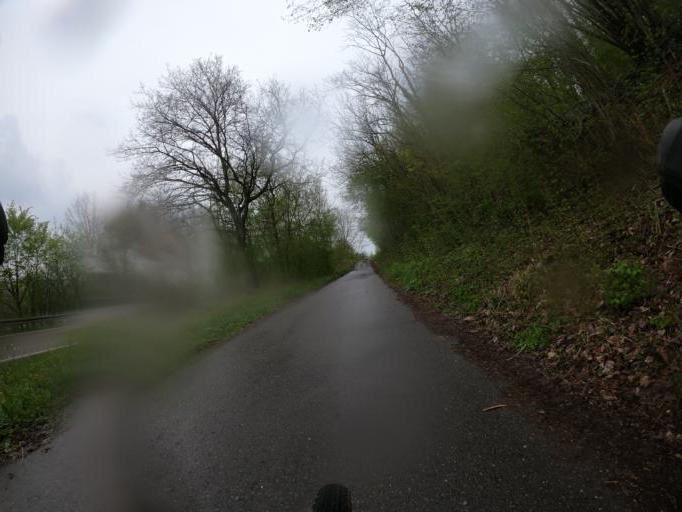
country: DE
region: Baden-Wuerttemberg
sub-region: Regierungsbezirk Stuttgart
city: Oberriexingen
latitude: 48.9270
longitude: 9.0340
